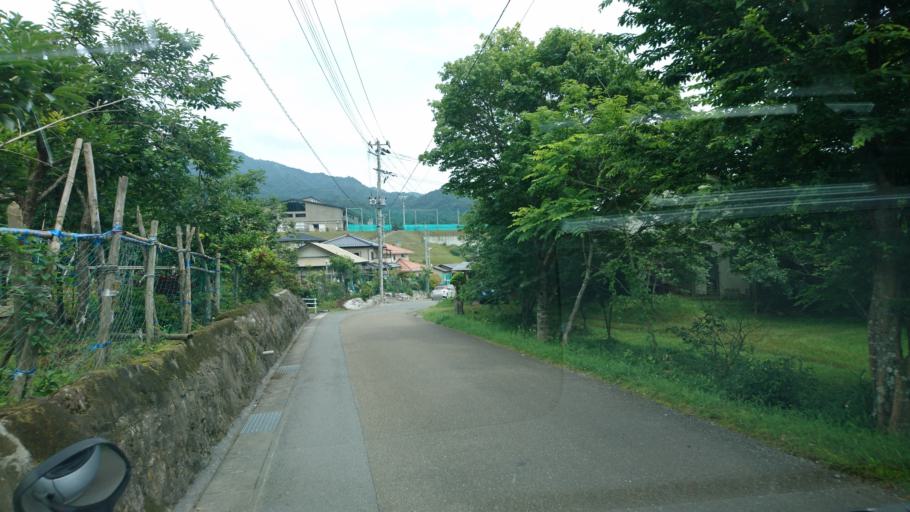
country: JP
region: Iwate
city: Ofunato
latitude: 39.1264
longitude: 141.8069
